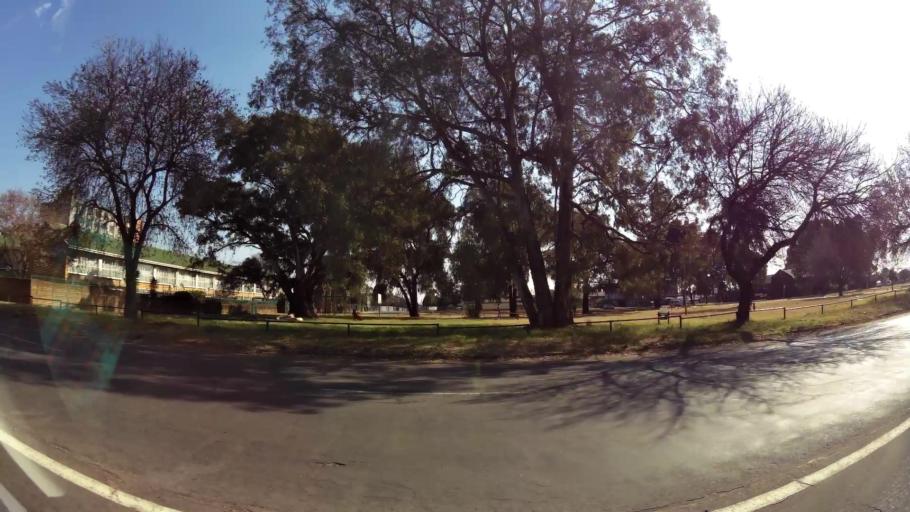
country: ZA
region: Gauteng
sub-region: City of Johannesburg Metropolitan Municipality
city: Modderfontein
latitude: -26.1208
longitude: 28.2326
